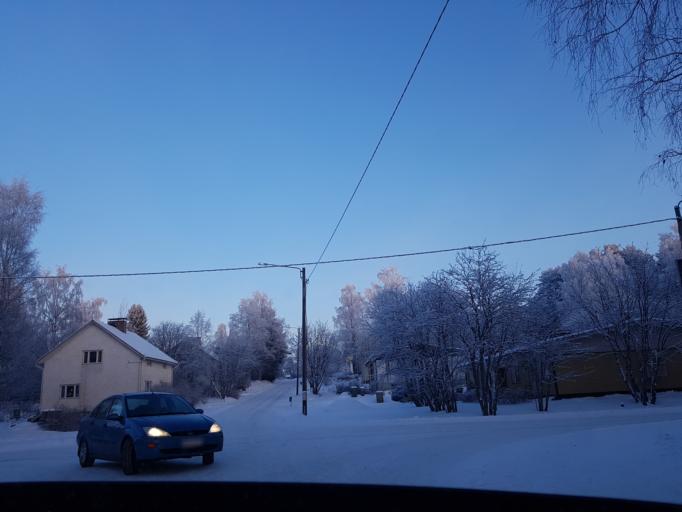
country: FI
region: Kainuu
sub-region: Kehys-Kainuu
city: Kuhmo
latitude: 64.1292
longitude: 29.5272
